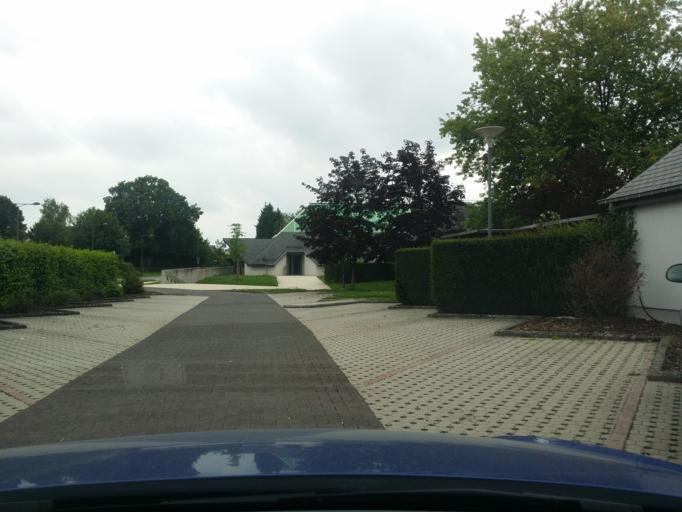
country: LU
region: Luxembourg
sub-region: Canton de Luxembourg
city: Bertrange
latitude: 49.6092
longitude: 6.0545
